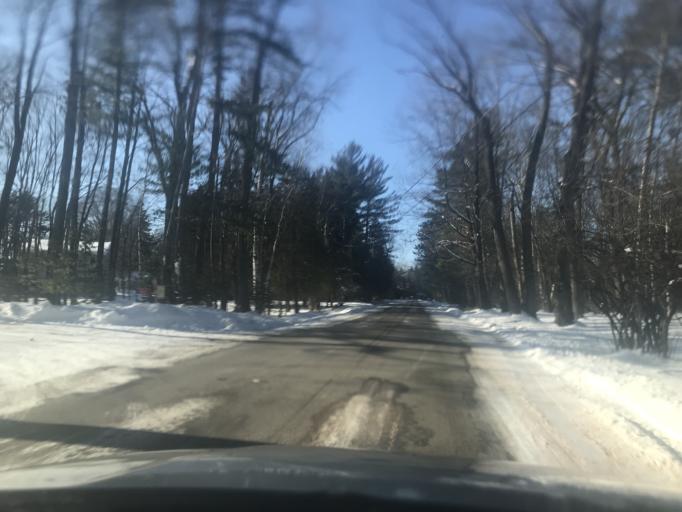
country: US
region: Wisconsin
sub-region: Marinette County
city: Marinette
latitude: 45.1197
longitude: -87.6651
